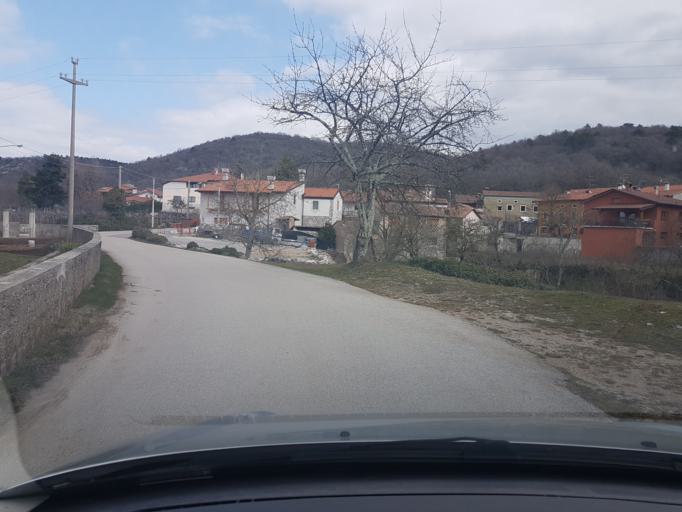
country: IT
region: Friuli Venezia Giulia
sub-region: Provincia di Trieste
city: Santa Croce
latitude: 45.7573
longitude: 13.7168
